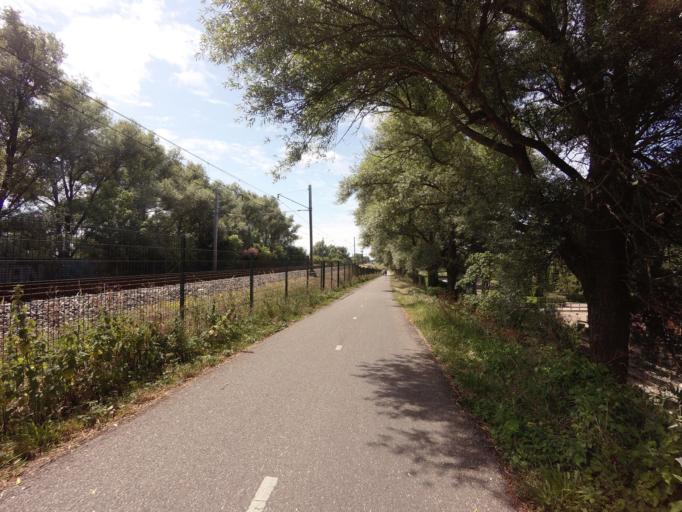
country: NL
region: South Holland
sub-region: Gemeente Teylingen
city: Sassenheim
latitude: 52.2205
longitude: 4.5425
